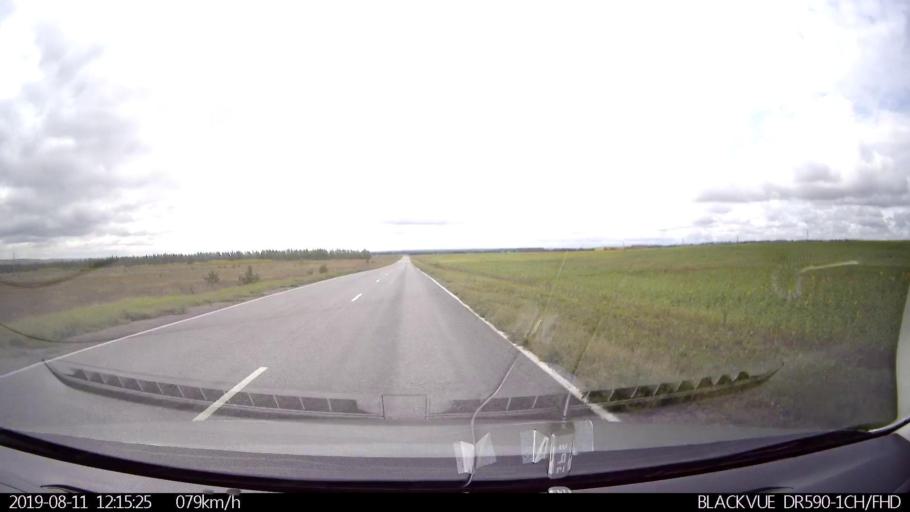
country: RU
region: Ulyanovsk
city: Ignatovka
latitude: 53.9419
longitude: 47.9687
